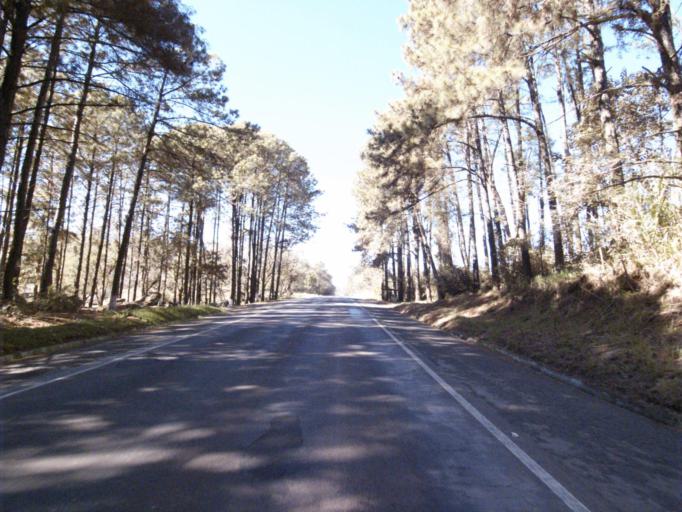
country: BR
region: Santa Catarina
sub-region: Sao Lourenco Do Oeste
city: Sao Lourenco dOeste
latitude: -26.7614
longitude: -53.2218
